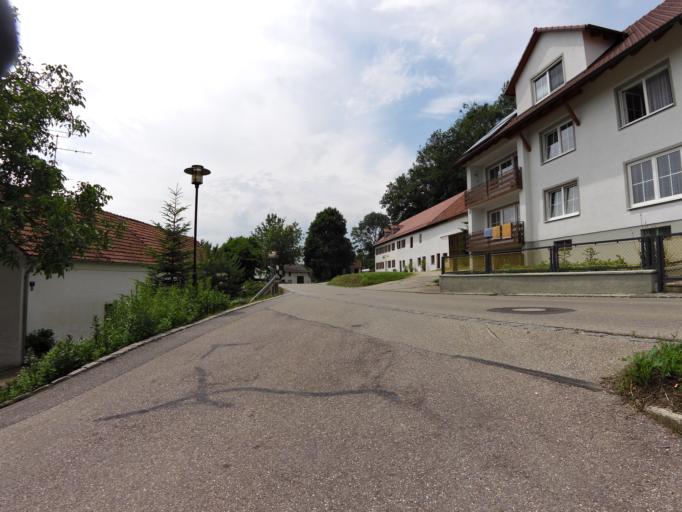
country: DE
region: Bavaria
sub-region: Upper Bavaria
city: Langenbach
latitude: 48.4613
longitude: 11.8630
